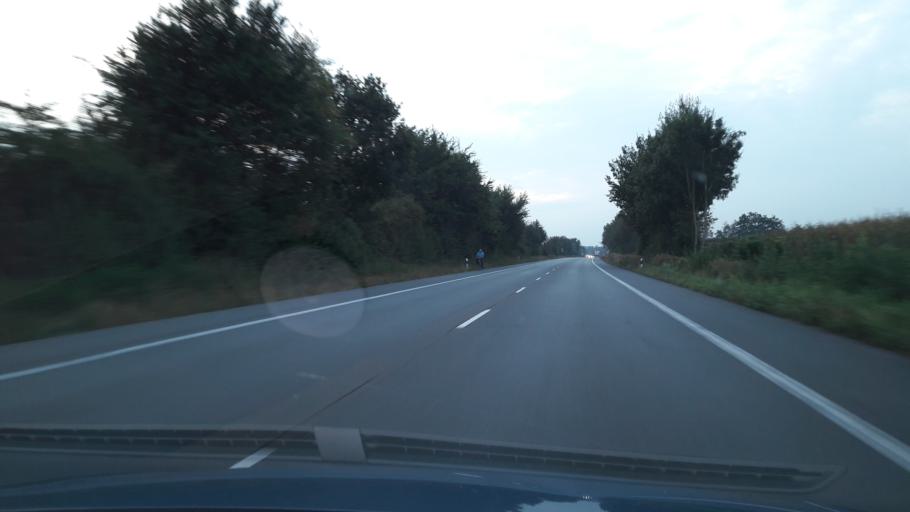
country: DE
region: North Rhine-Westphalia
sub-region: Regierungsbezirk Munster
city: Telgte
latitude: 51.9329
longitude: 7.7440
